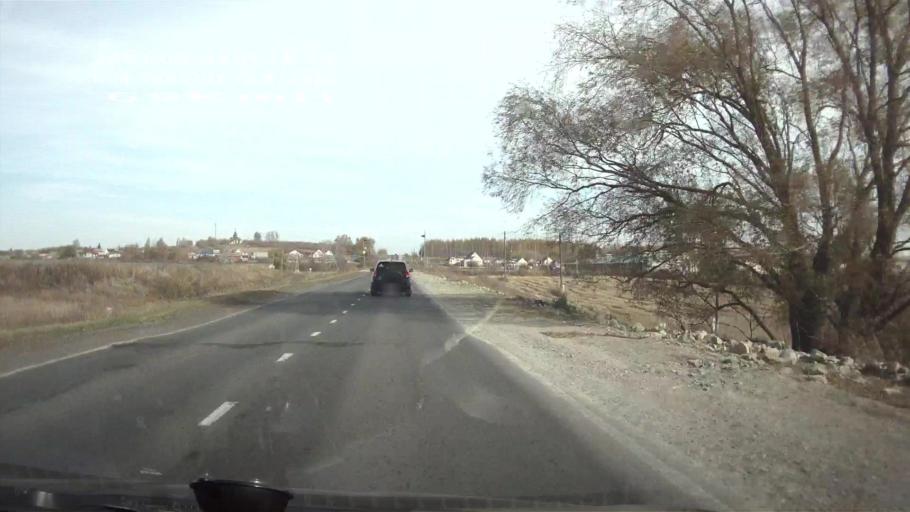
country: RU
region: Mordoviya
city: Atyashevo
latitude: 54.5597
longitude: 45.9749
